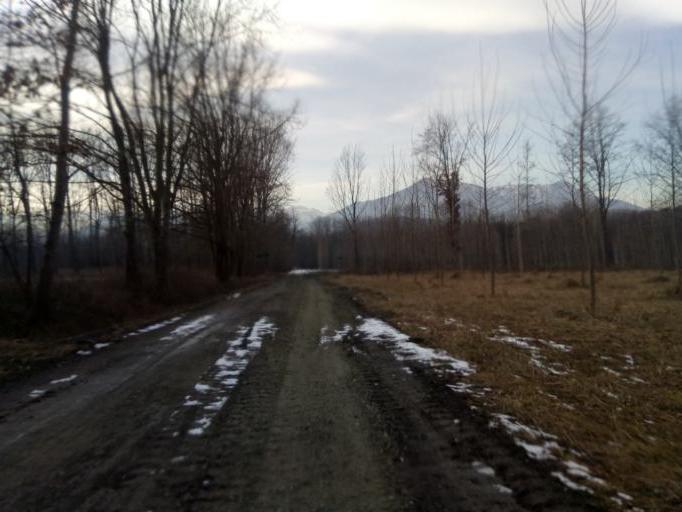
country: IT
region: Piedmont
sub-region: Provincia di Torino
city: Cascinette d'Ivrea
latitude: 45.4854
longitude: 7.9180
